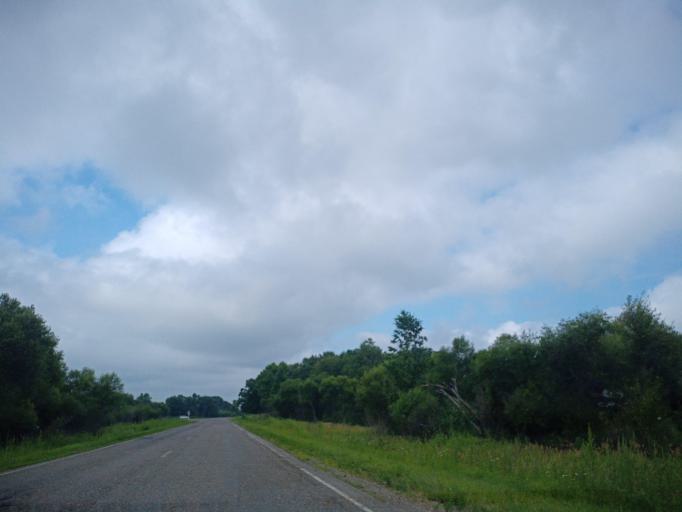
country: RU
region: Primorskiy
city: Dal'nerechensk
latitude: 45.9387
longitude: 133.8707
